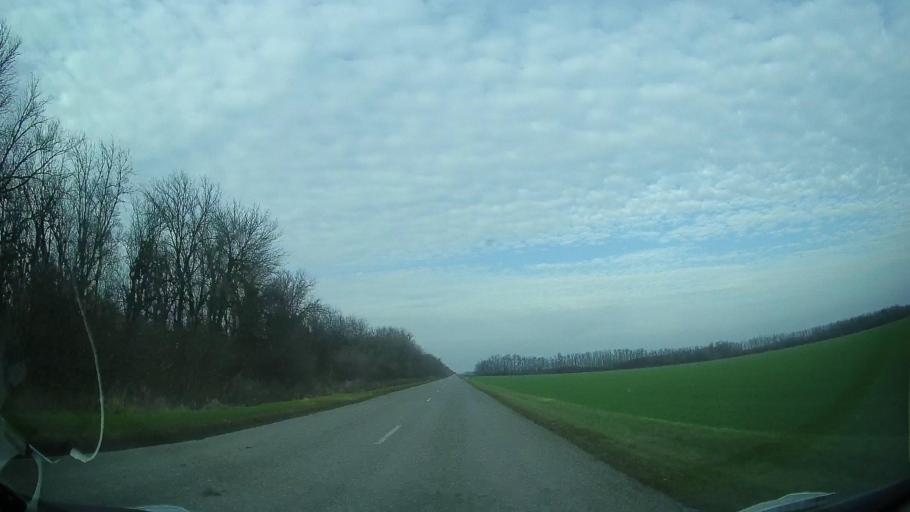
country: RU
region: Rostov
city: Zernograd
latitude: 46.9838
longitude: 40.3916
